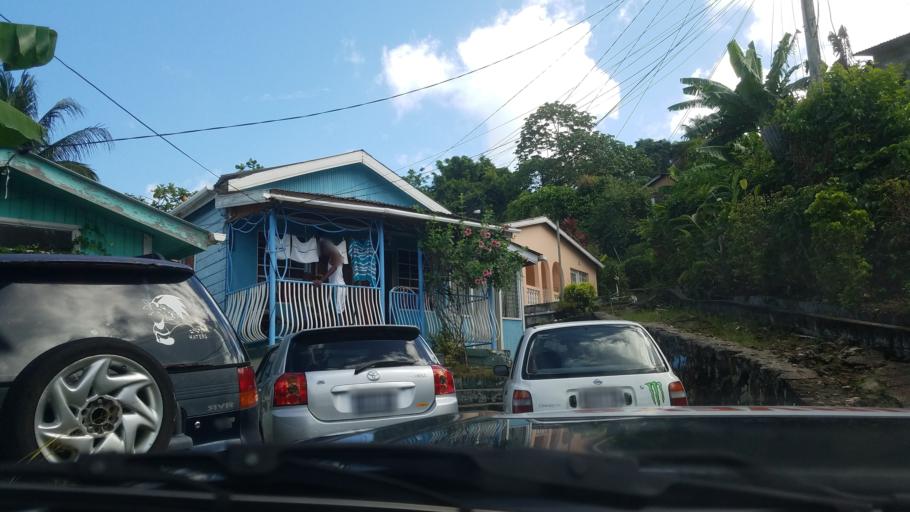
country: LC
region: Castries Quarter
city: Bisee
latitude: 14.0197
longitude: -60.9809
